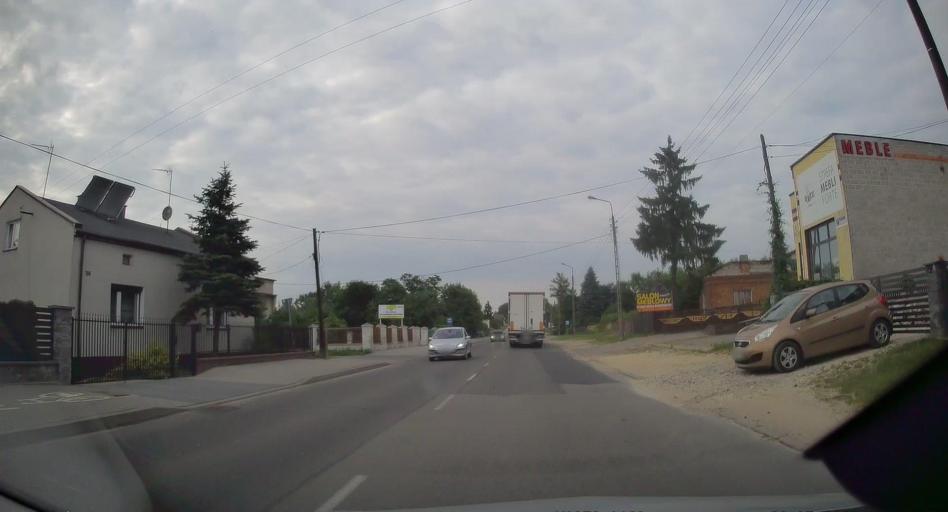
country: PL
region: Lodz Voivodeship
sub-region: Powiat radomszczanski
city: Radomsko
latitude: 51.0484
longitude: 19.4390
